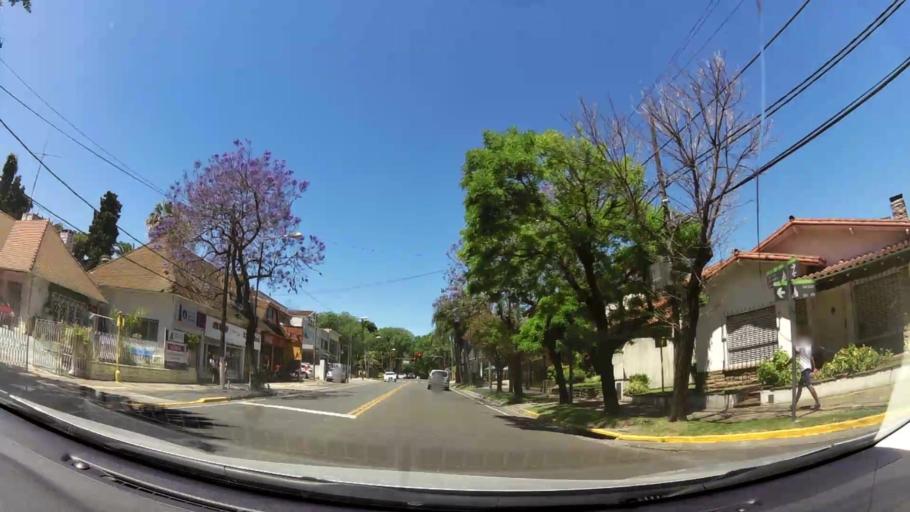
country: AR
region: Buenos Aires
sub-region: Partido de Tigre
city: Tigre
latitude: -34.4471
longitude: -58.5432
